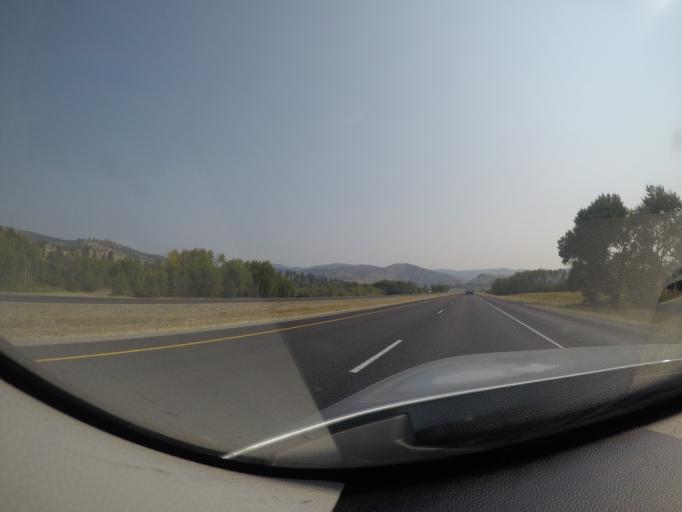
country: US
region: Montana
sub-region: Granite County
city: Philipsburg
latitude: 46.7000
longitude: -113.3468
